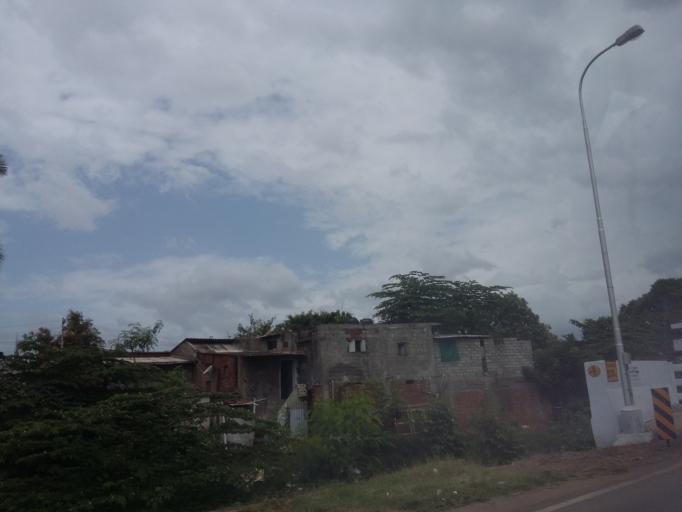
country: IN
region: Tamil Nadu
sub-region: Coimbatore
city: Perur
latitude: 11.0226
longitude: 76.9130
